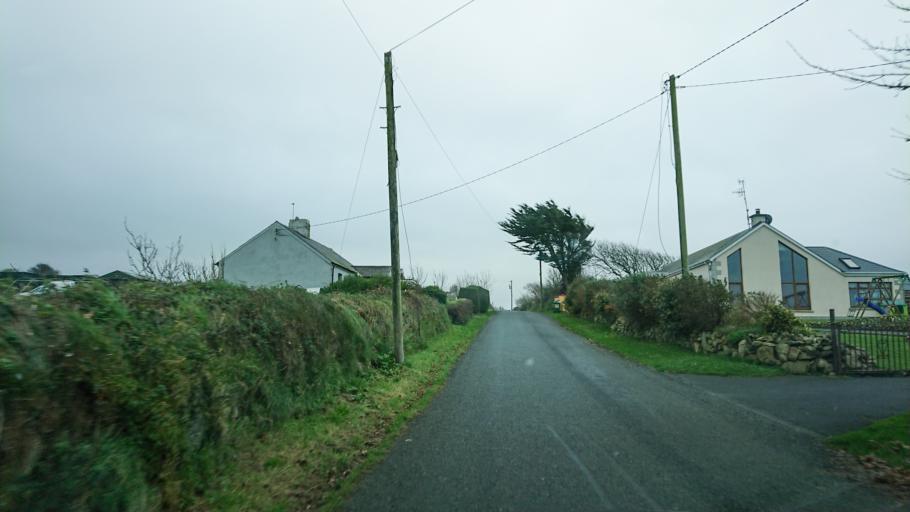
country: IE
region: Munster
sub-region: Waterford
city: Tra Mhor
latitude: 52.1400
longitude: -7.2321
